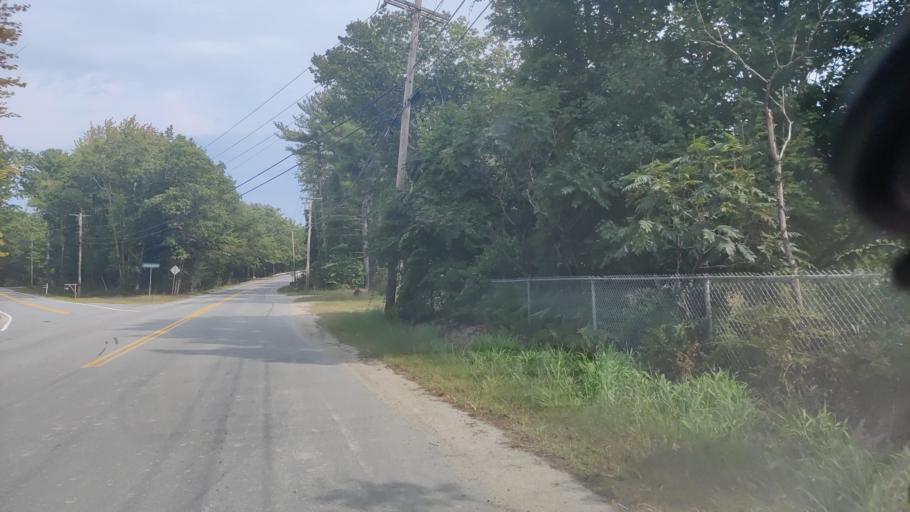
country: US
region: Maine
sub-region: Cumberland County
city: Cumberland Center
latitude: 43.8124
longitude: -70.3210
